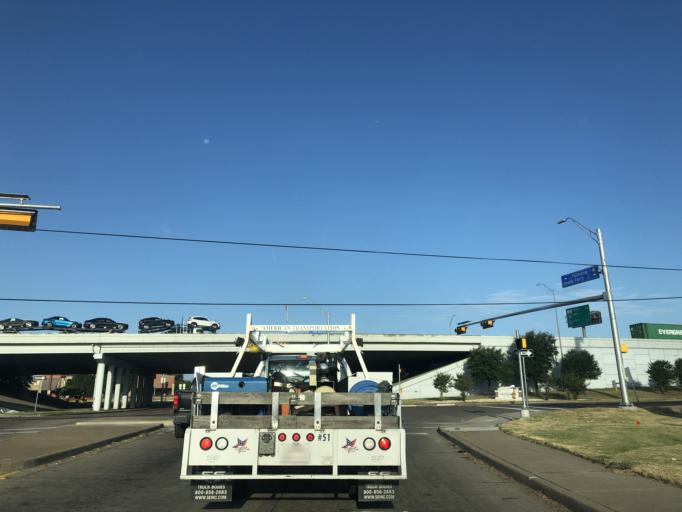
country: US
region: Texas
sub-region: Dallas County
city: Hutchins
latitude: 32.6493
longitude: -96.7069
